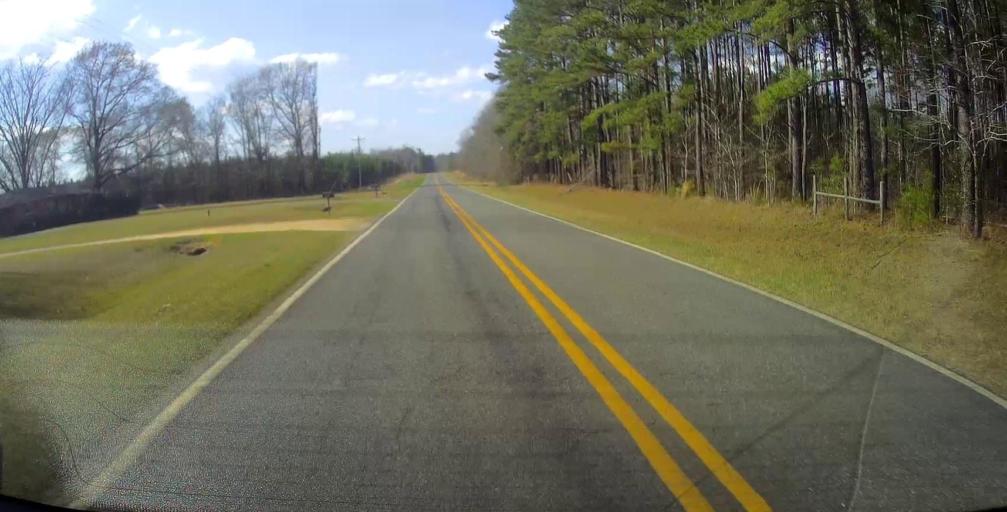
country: US
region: Georgia
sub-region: Laurens County
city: Dublin
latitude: 32.5898
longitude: -83.0628
